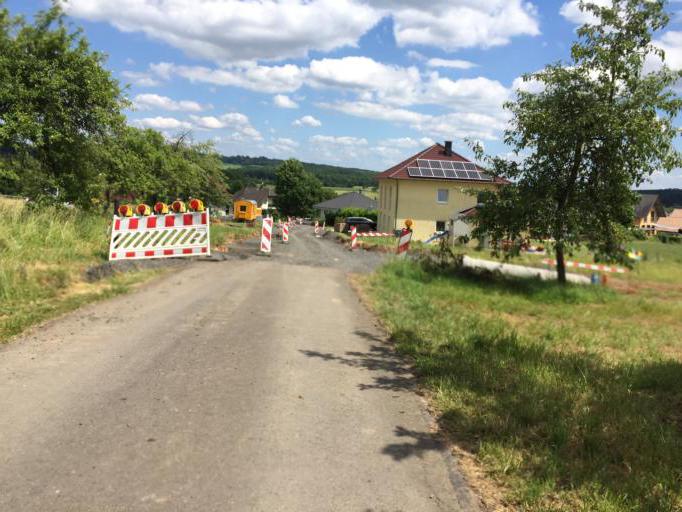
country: DE
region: Rheinland-Pfalz
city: Berod bei Wallmerod
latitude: 50.4761
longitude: 7.9195
